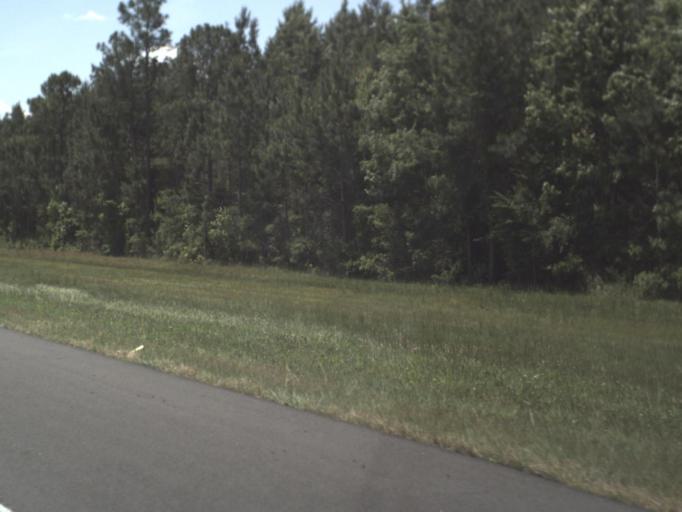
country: US
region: Florida
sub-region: Nassau County
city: Yulee
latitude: 30.6385
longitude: -81.6569
